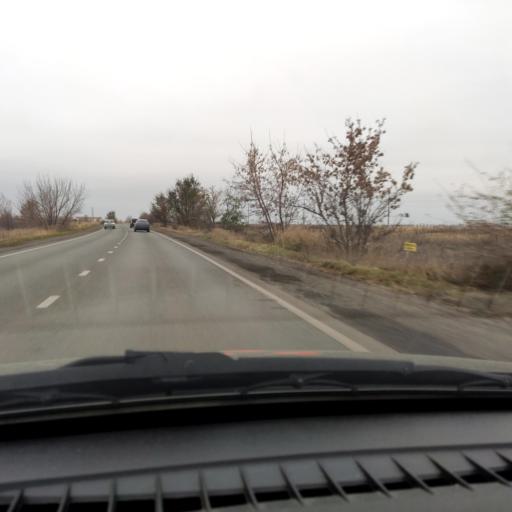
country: RU
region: Samara
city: Podstepki
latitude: 53.5180
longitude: 49.2105
